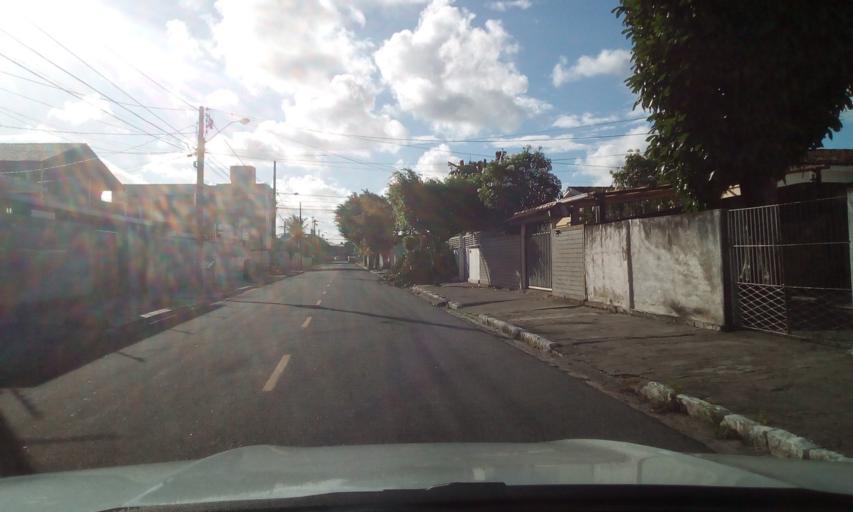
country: BR
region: Paraiba
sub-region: Joao Pessoa
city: Joao Pessoa
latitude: -7.1154
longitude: -34.8642
